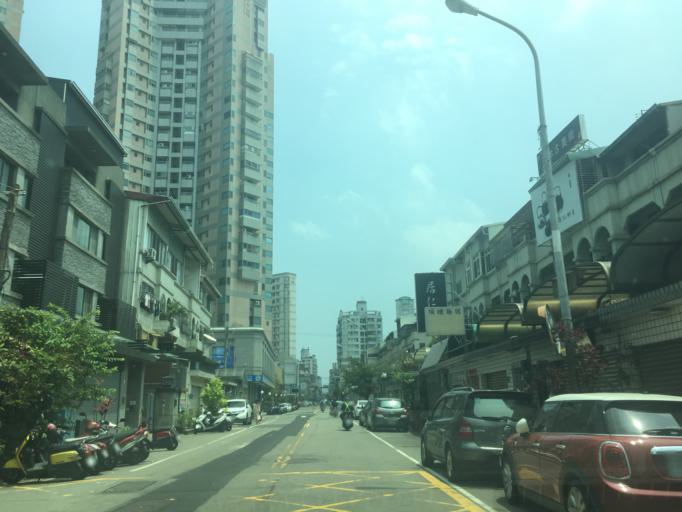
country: TW
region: Taiwan
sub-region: Taichung City
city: Taichung
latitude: 24.1774
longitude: 120.6863
